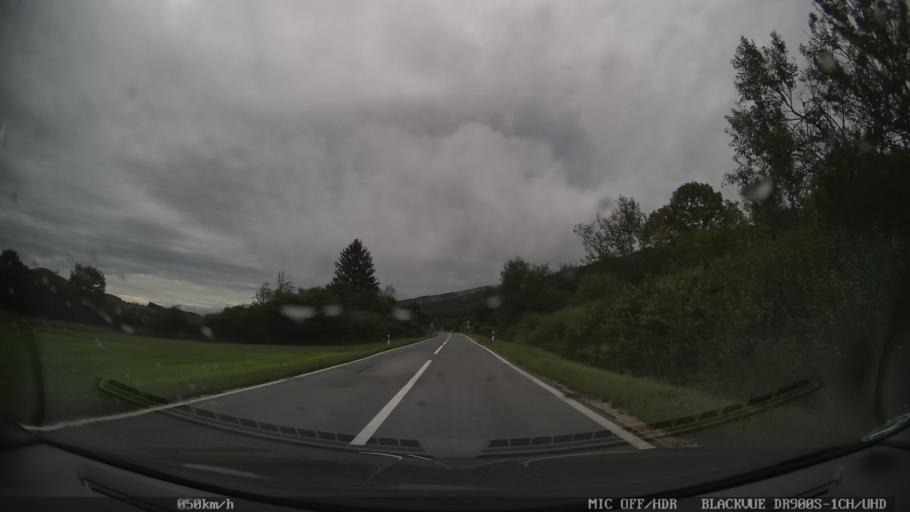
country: HR
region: Licko-Senjska
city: Brinje
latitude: 44.9428
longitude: 15.1258
